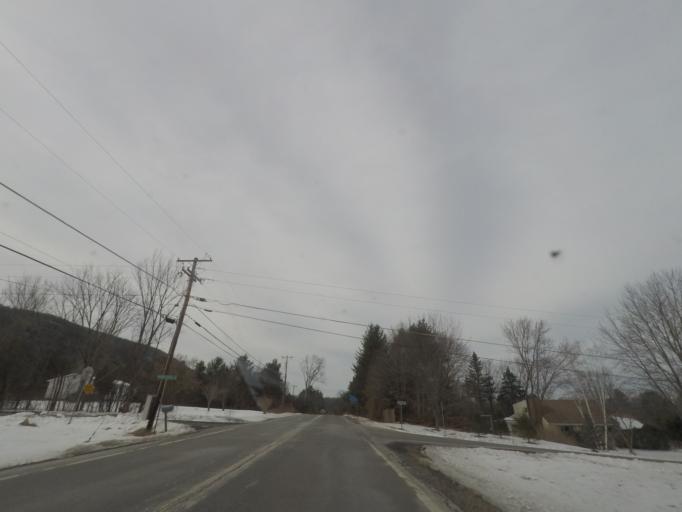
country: US
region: New York
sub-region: Albany County
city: Altamont
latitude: 42.6670
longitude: -74.0043
